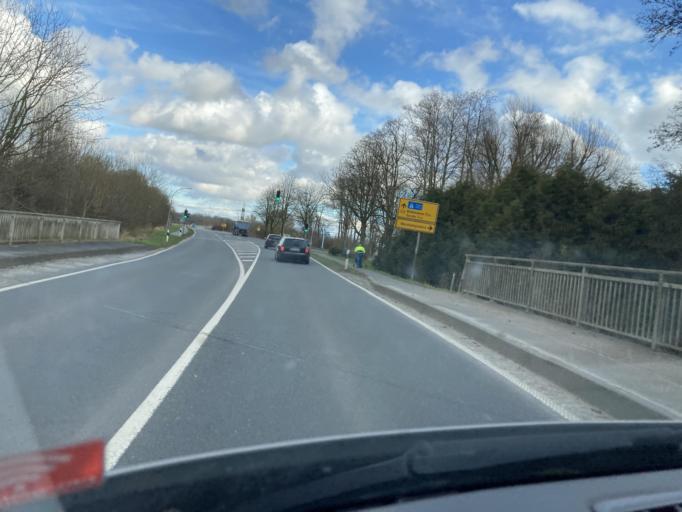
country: DE
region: Lower Saxony
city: Sande
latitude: 53.4827
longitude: 7.9891
